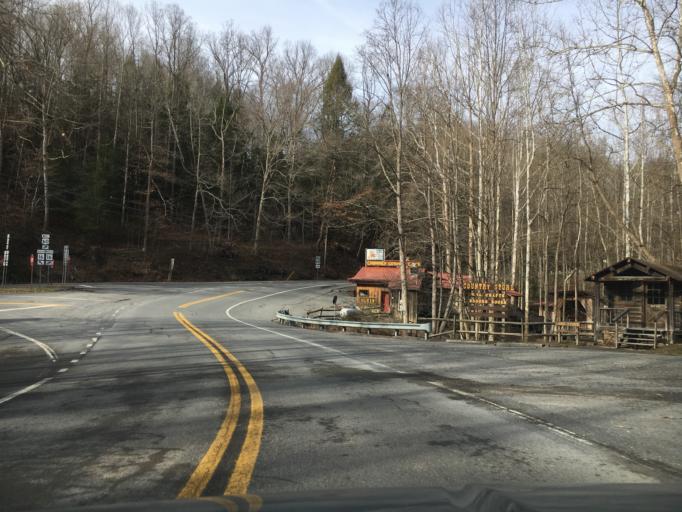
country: US
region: West Virginia
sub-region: Fayette County
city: Ansted
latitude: 38.1385
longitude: -81.1465
